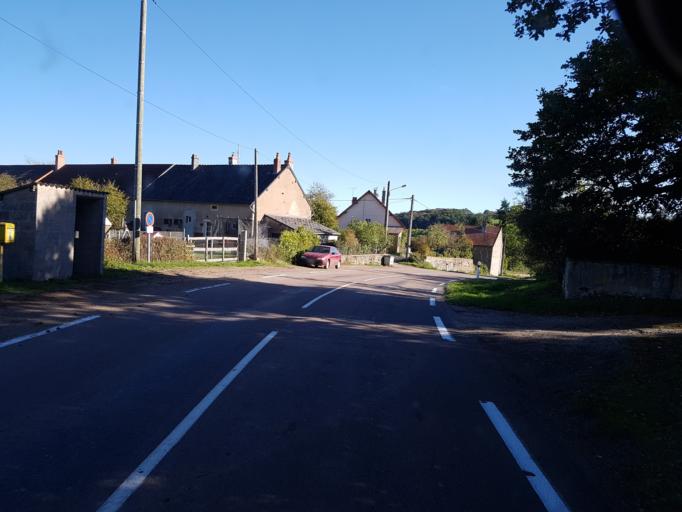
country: FR
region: Bourgogne
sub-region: Departement de Saone-et-Loire
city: Autun
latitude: 47.0544
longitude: 4.2660
